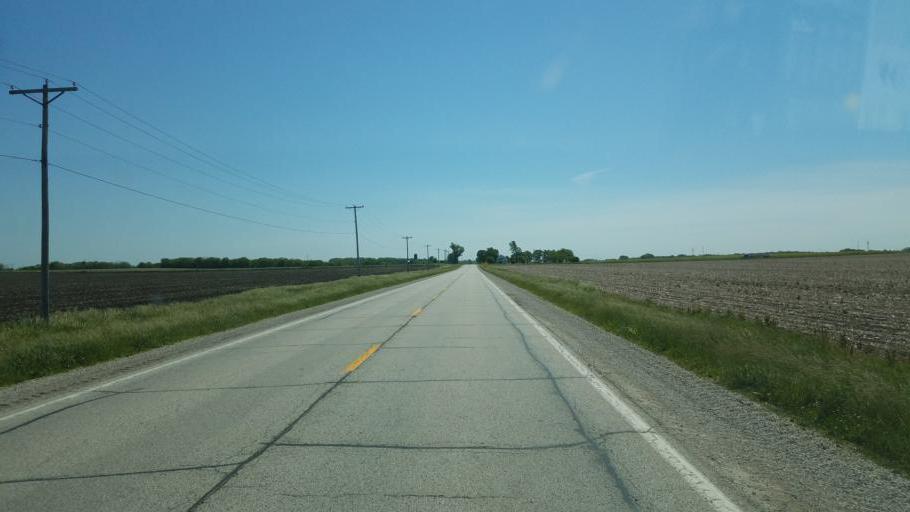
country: US
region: Illinois
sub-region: McLean County
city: Heyworth
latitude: 40.3121
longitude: -89.0415
